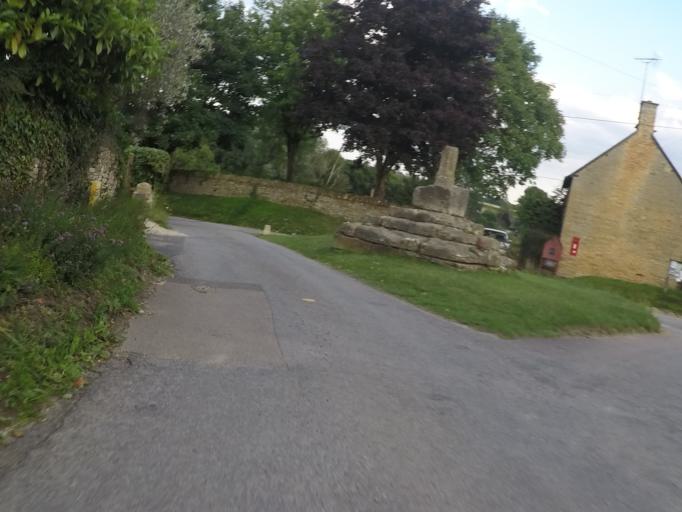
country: GB
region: England
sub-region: Oxfordshire
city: Charlbury
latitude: 51.8961
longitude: -1.4792
